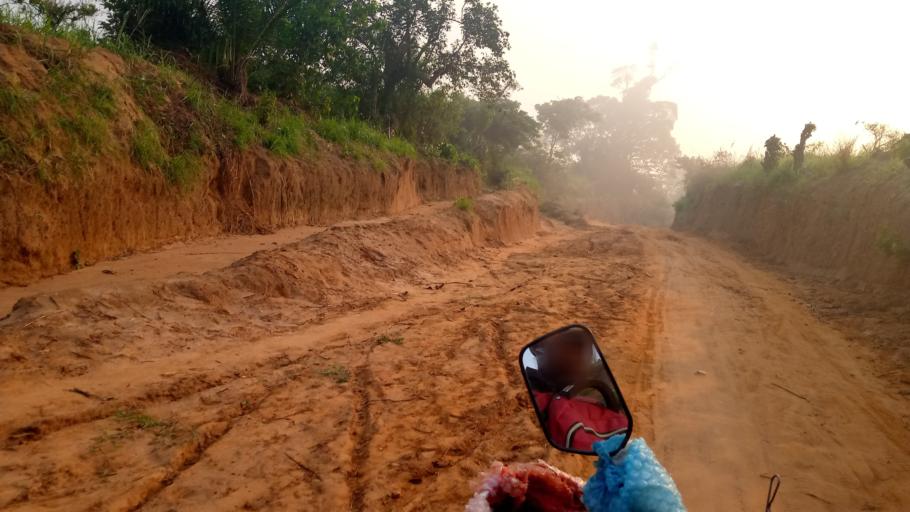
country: CD
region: Bandundu
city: Kikwit
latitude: -4.8436
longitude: 18.7191
